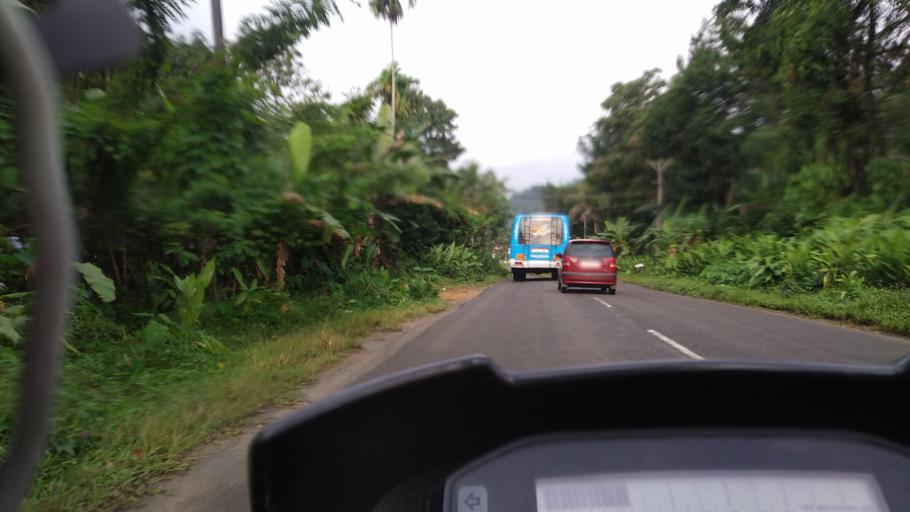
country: IN
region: Kerala
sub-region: Idukki
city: Kuttampuzha
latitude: 10.0502
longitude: 76.7511
